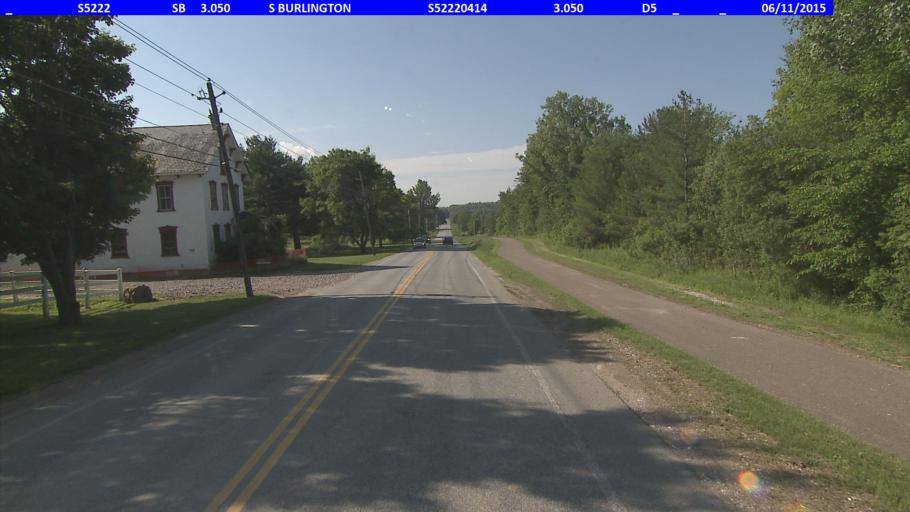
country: US
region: Vermont
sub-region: Chittenden County
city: South Burlington
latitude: 44.4603
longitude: -73.1903
